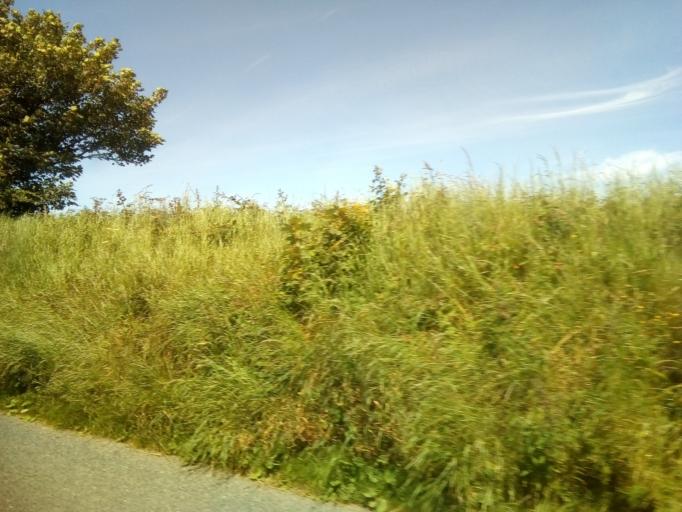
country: IE
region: Leinster
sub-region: Loch Garman
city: Loch Garman
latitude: 52.2343
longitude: -6.5737
